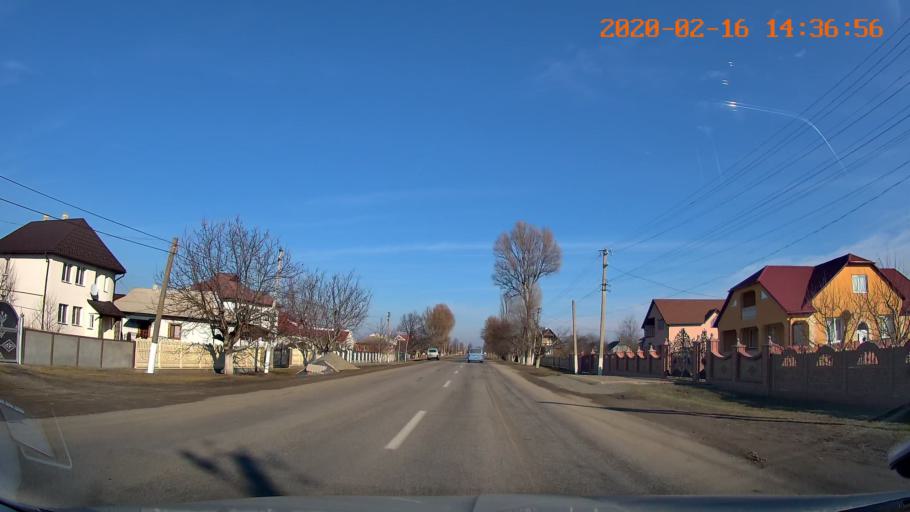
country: RO
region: Botosani
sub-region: Comuna Darabani
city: Bajura
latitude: 48.2262
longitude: 26.5166
